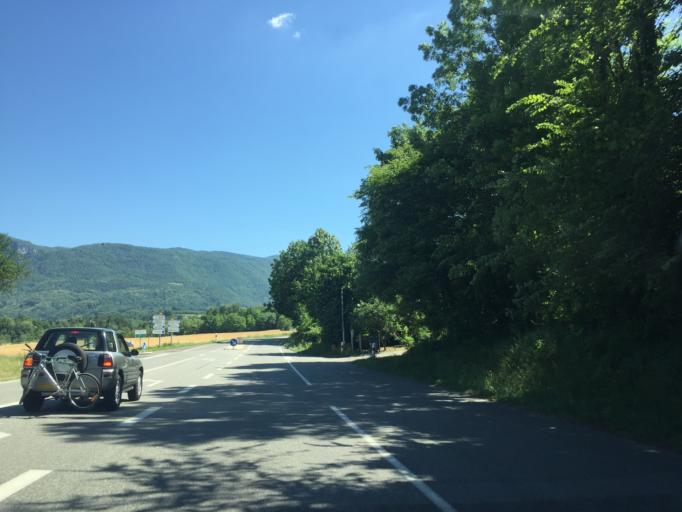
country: FR
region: Rhone-Alpes
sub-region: Departement de la Drome
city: Saint-Jean-en-Royans
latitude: 45.0450
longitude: 5.2974
